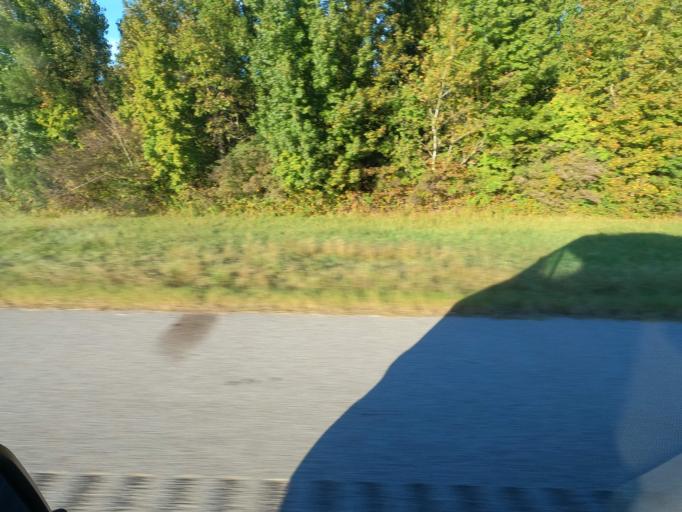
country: US
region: Tennessee
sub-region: Shelby County
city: Millington
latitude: 35.3133
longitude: -89.8630
